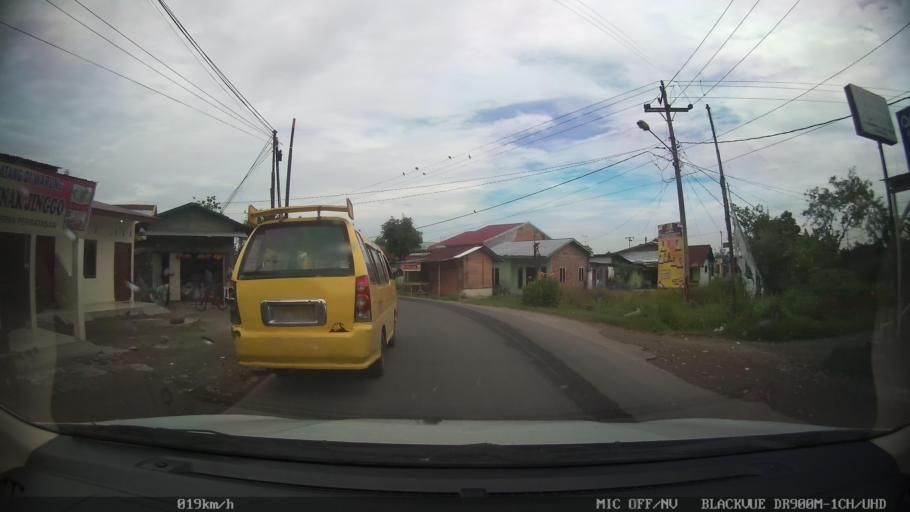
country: ID
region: North Sumatra
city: Sunggal
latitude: 3.6199
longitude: 98.6010
